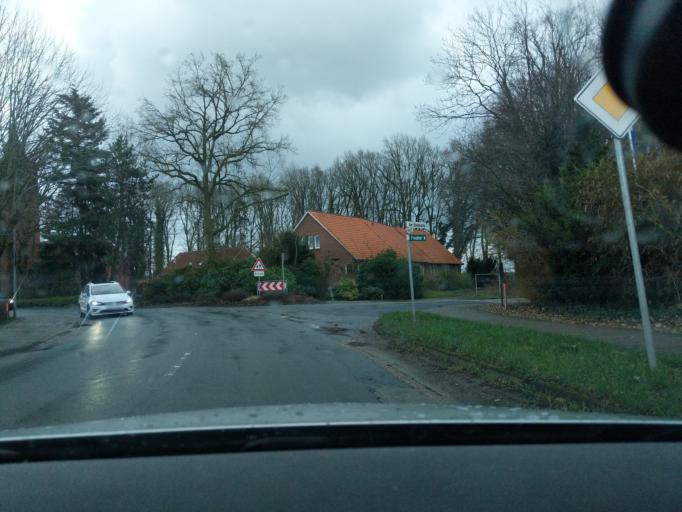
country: DE
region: Lower Saxony
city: Deinste
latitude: 53.5249
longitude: 9.4172
